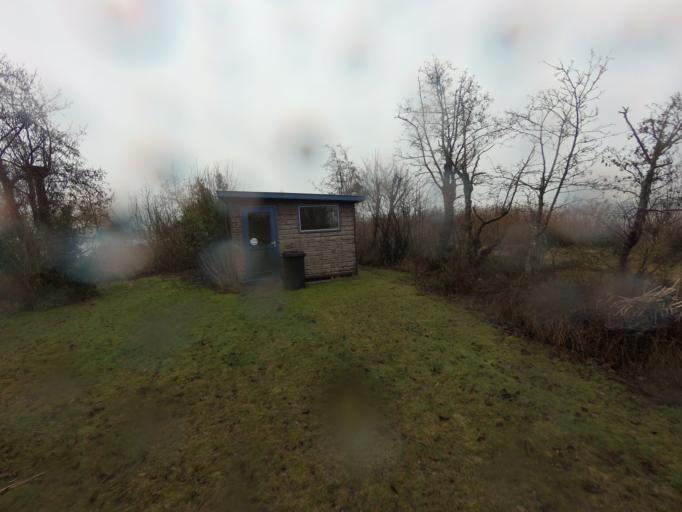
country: NL
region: South Holland
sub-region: Gemeente Vlist
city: Haastrecht
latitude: 52.0232
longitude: 4.7535
